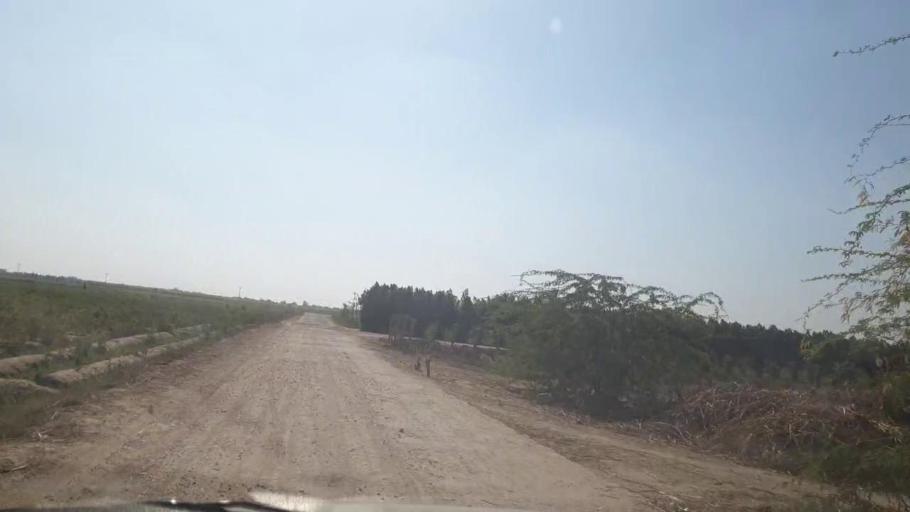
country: PK
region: Sindh
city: Mirpur Khas
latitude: 25.4778
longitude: 69.1311
